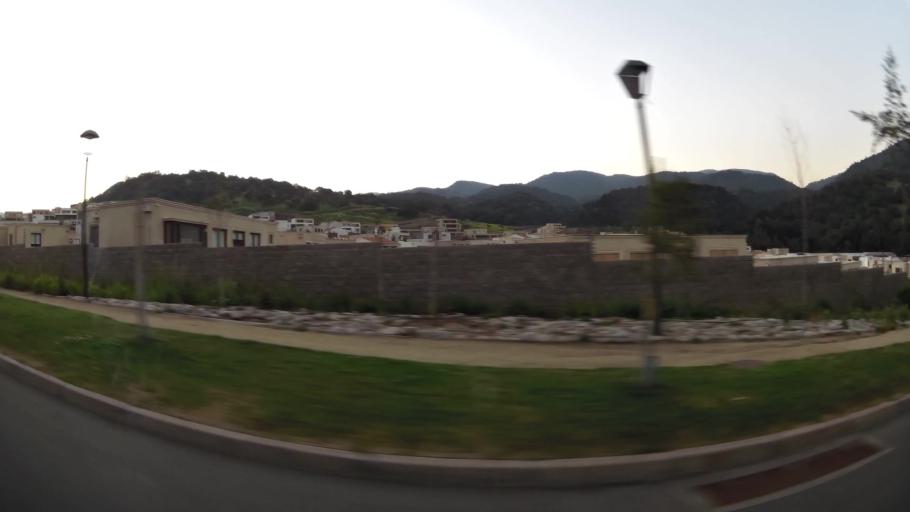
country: CL
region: Santiago Metropolitan
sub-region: Provincia de Chacabuco
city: Chicureo Abajo
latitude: -33.3152
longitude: -70.5451
